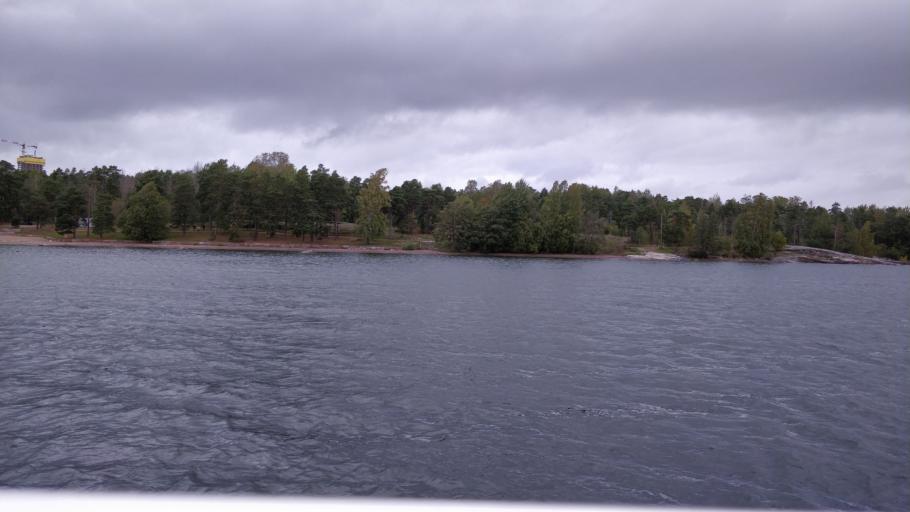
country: FI
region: Uusimaa
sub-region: Helsinki
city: Helsinki
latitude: 60.1776
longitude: 24.9960
